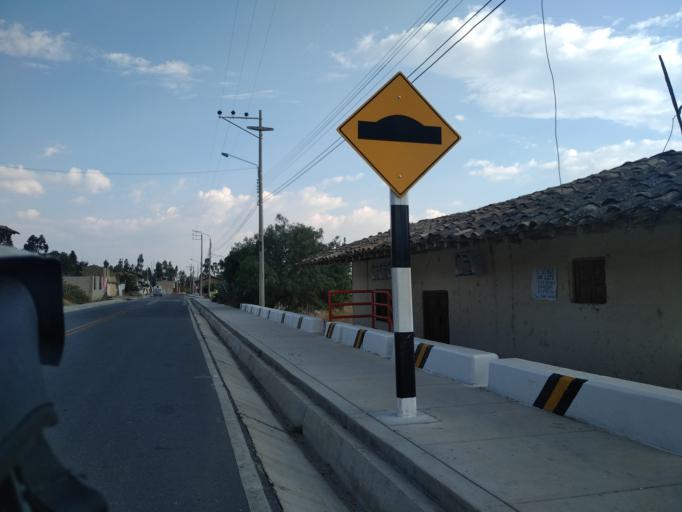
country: PE
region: Cajamarca
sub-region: San Marcos
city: La Grama
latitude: -7.3899
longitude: -78.1242
